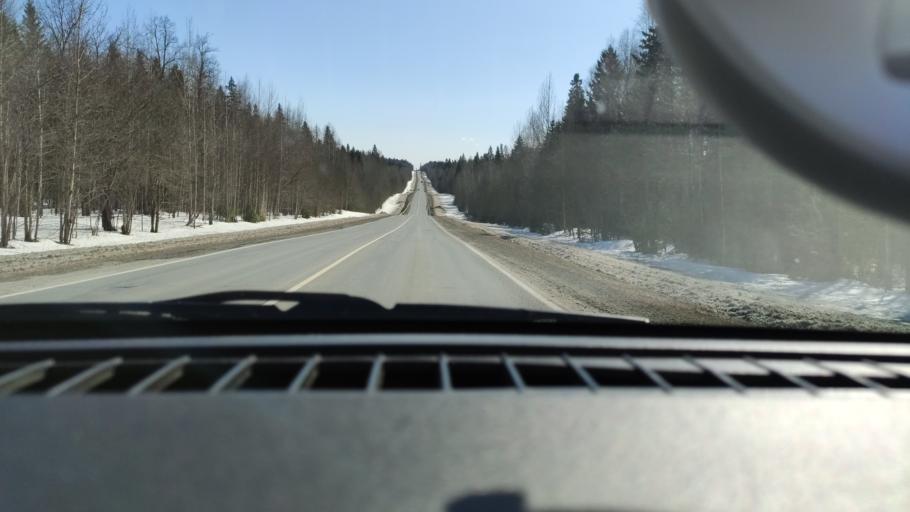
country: RU
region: Perm
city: Perm
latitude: 58.1678
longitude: 56.2379
